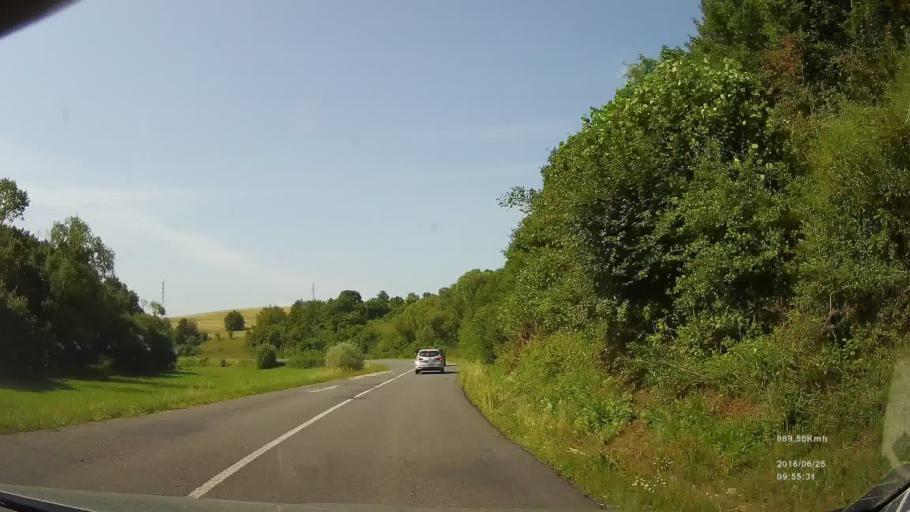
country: SK
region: Banskobystricky
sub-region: Okres Banska Bystrica
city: Banska Bystrica
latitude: 48.6850
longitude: 19.2181
